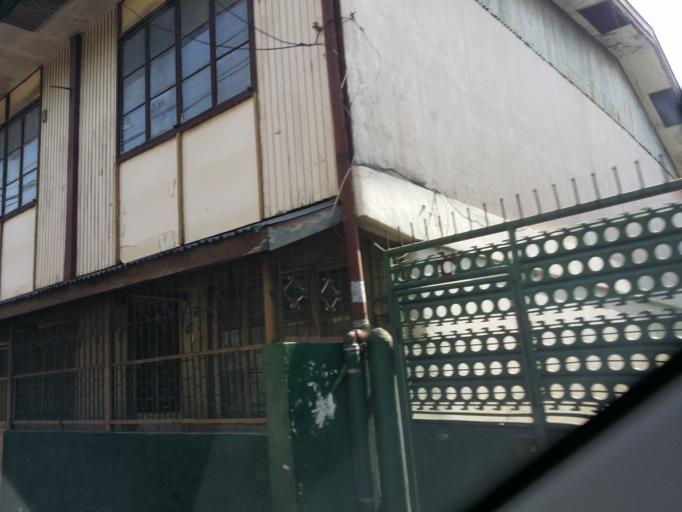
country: PH
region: Metro Manila
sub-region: Mandaluyong
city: Mandaluyong City
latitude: 14.5835
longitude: 121.0213
